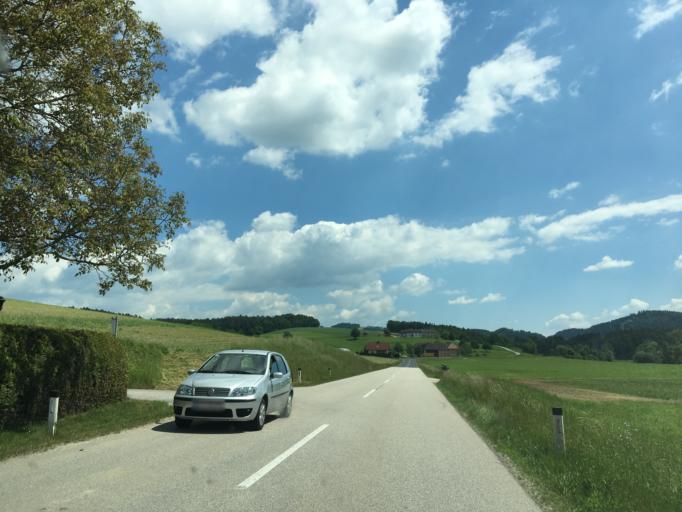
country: AT
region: Upper Austria
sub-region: Politischer Bezirk Perg
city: Perg
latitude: 48.3189
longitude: 14.6016
